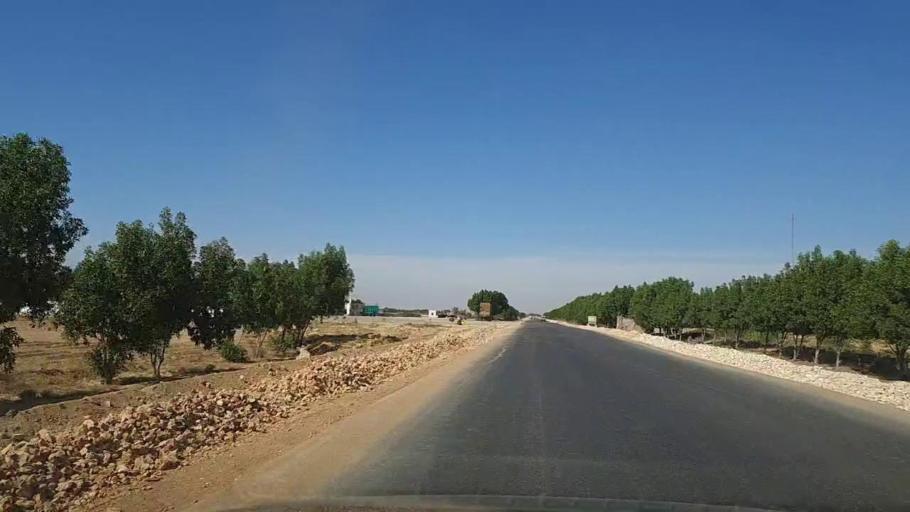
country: PK
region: Sindh
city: Kotri
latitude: 25.2672
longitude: 68.2191
